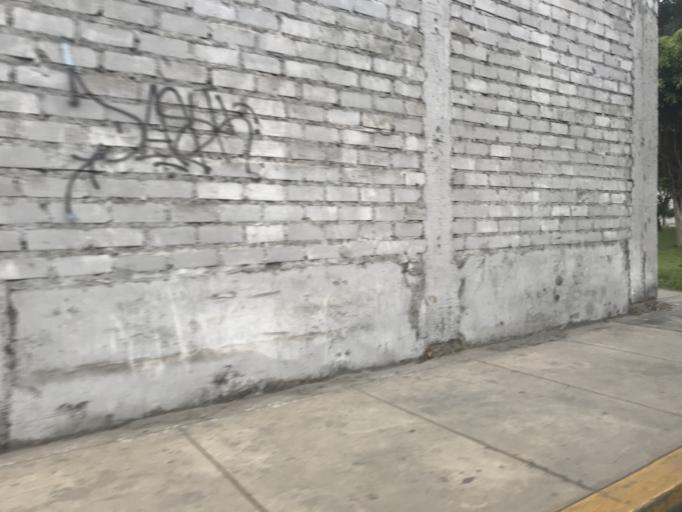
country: PE
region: Callao
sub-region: Callao
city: Callao
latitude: -12.0674
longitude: -77.0928
